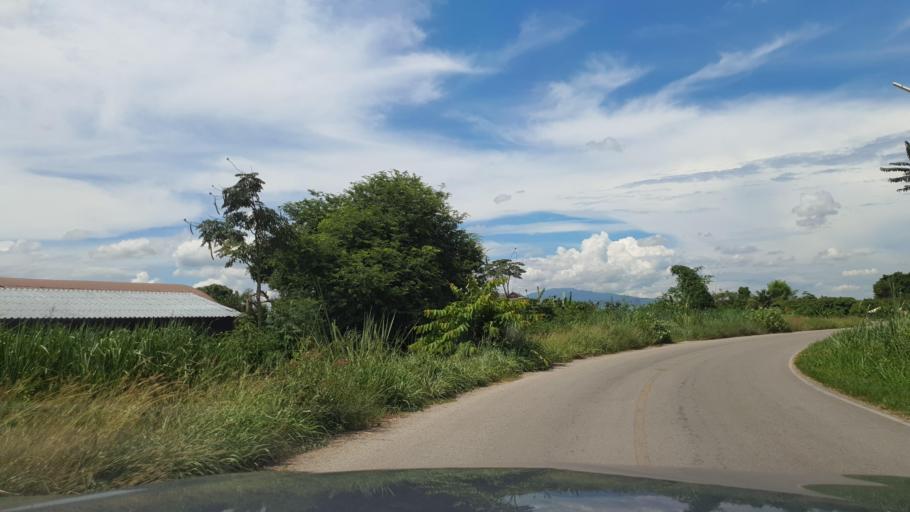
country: TH
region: Chiang Mai
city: San Pa Tong
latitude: 18.5898
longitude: 98.9054
